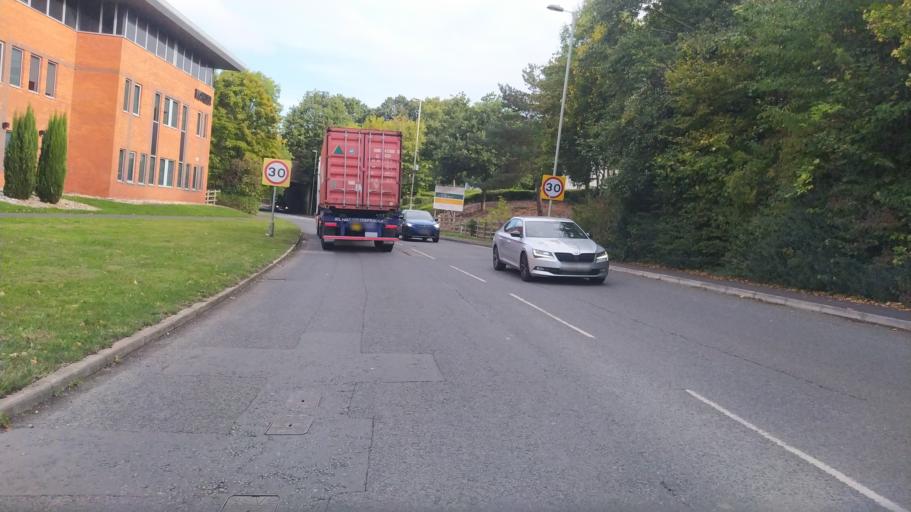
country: GB
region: England
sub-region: Hampshire
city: Hook
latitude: 51.2796
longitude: -0.9520
